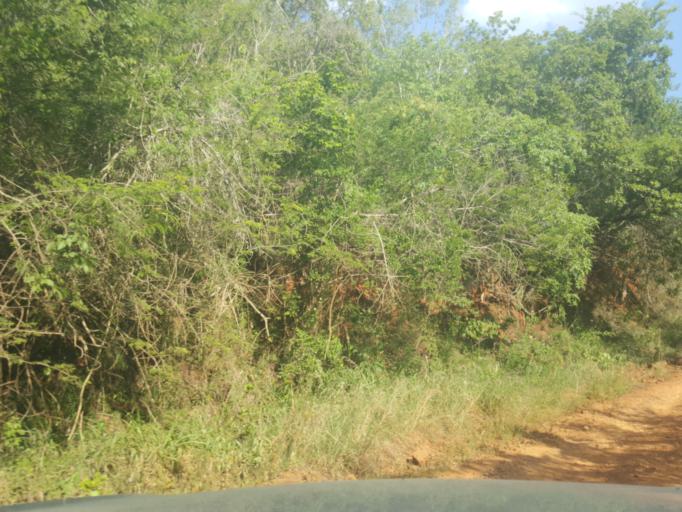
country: ZA
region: Limpopo
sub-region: Mopani District Municipality
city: Hoedspruit
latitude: -24.5913
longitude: 30.8365
